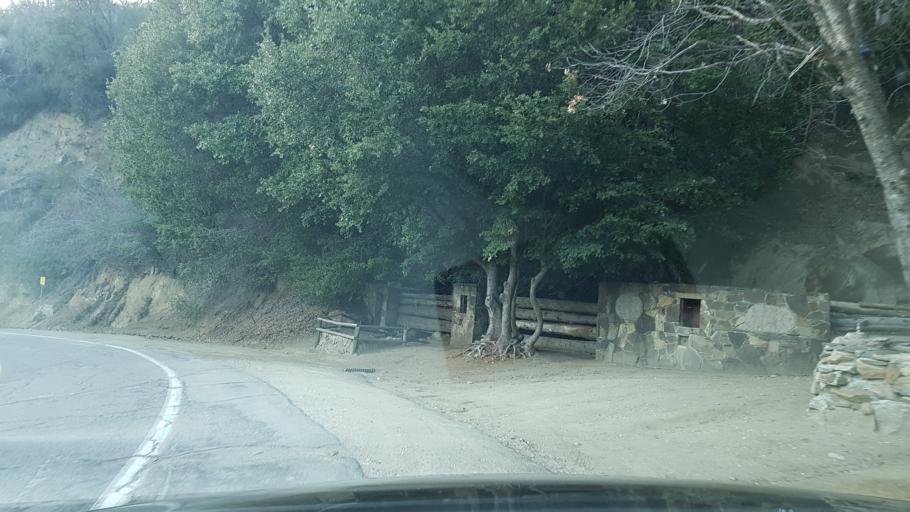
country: US
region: California
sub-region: Riverside County
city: Aguanga
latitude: 33.3143
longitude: -116.8705
